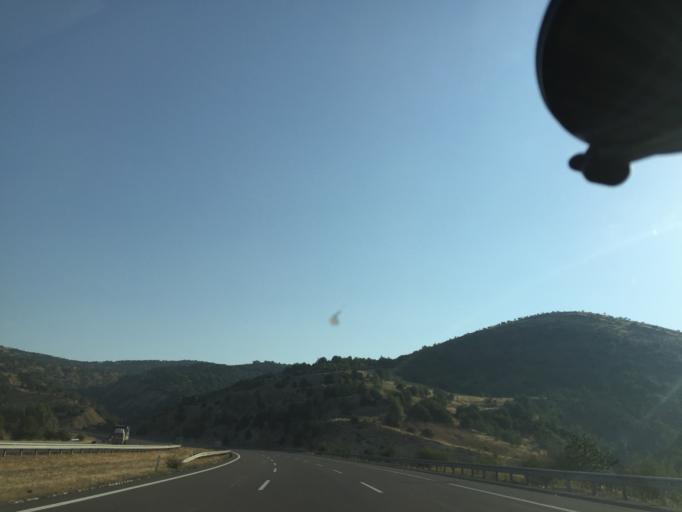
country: TR
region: Ankara
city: Celtikci
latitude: 40.3722
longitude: 32.4697
